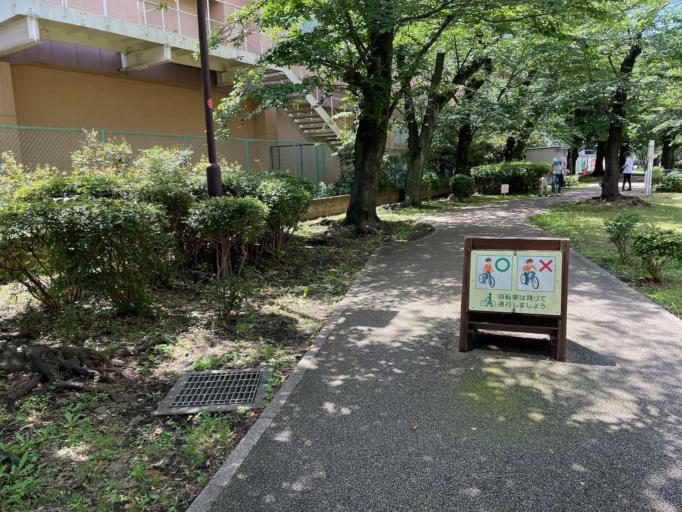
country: JP
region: Tokyo
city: Tokyo
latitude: 35.6484
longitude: 139.6326
